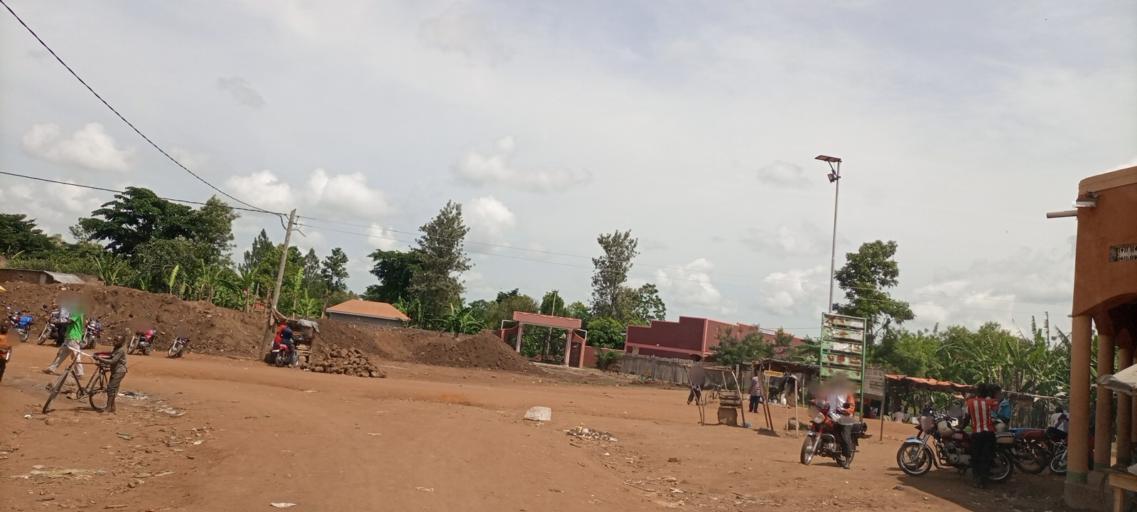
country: UG
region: Eastern Region
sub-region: Budaka District
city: Budaka
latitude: 1.1719
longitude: 33.9334
